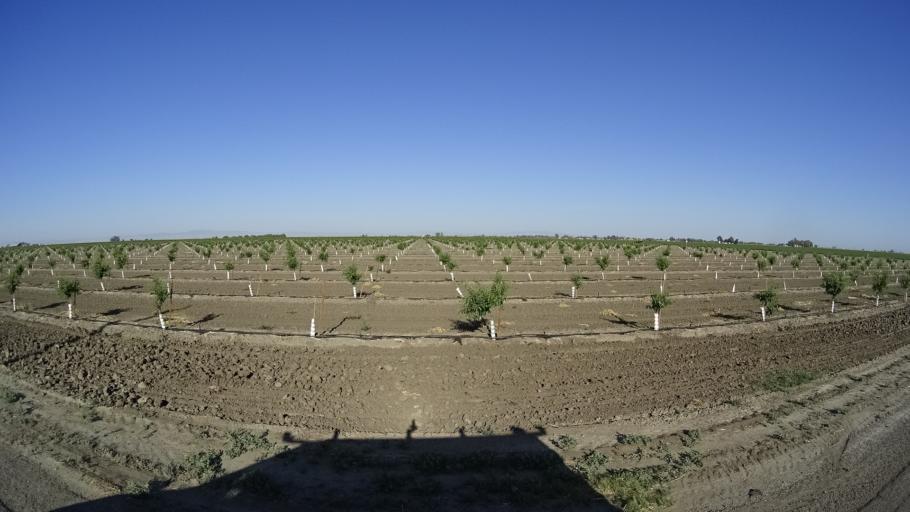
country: US
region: California
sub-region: Kings County
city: Stratford
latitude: 36.1813
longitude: -119.7984
